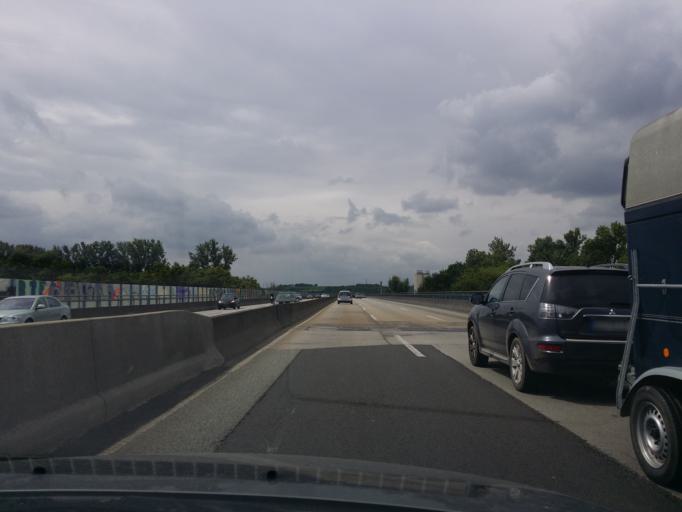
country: DE
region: Hesse
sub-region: Regierungsbezirk Darmstadt
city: Ginsheim-Gustavsburg
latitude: 49.9781
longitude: 8.3283
